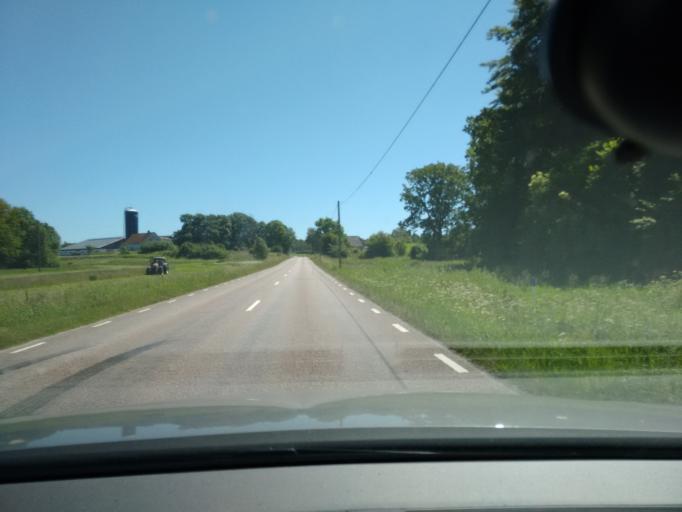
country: SE
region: Skane
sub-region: Horby Kommun
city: Hoerby
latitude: 55.7983
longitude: 13.8042
